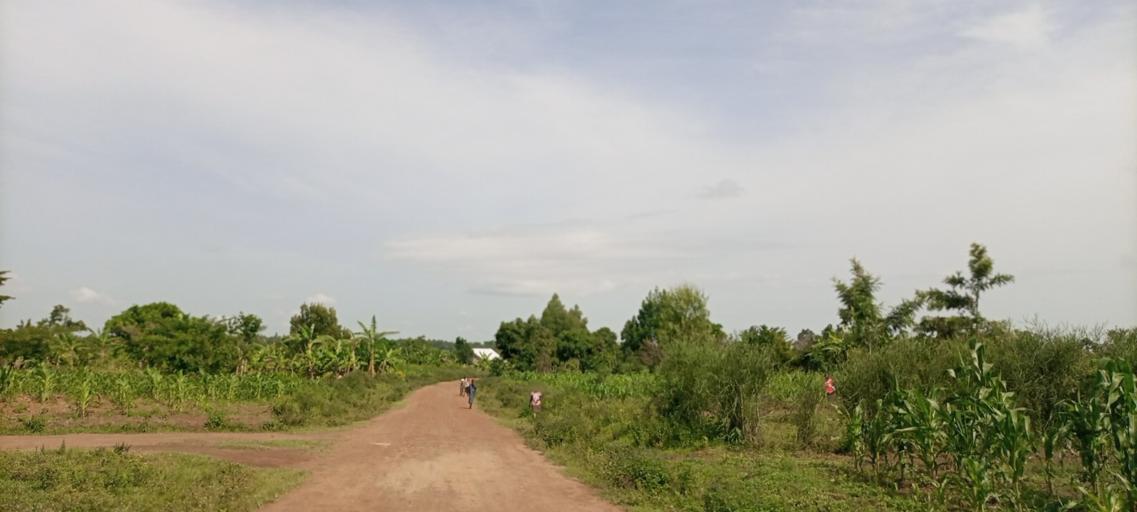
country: UG
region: Eastern Region
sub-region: Mbale District
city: Mbale
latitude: 1.1291
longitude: 34.0397
